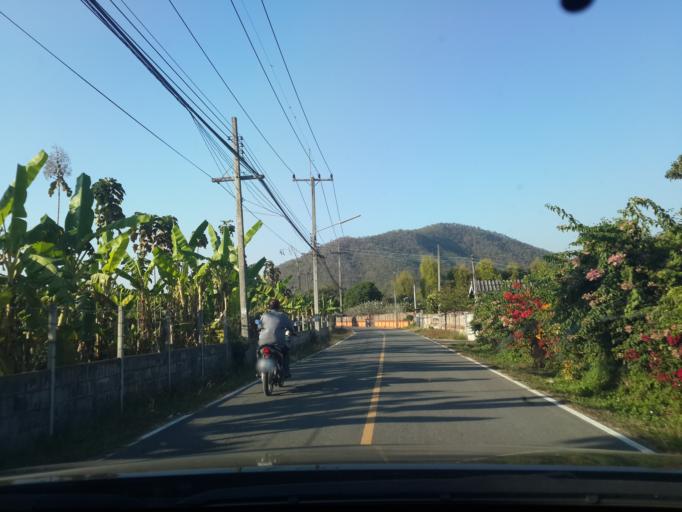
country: TH
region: Chiang Mai
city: San Sai
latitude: 18.9176
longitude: 99.1325
